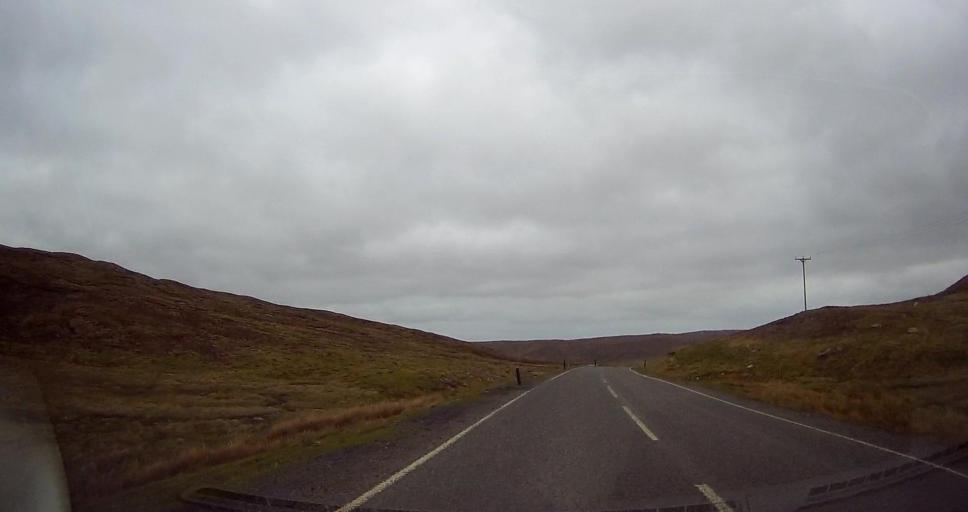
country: GB
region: Scotland
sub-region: Shetland Islands
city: Lerwick
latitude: 60.3432
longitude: -1.2969
